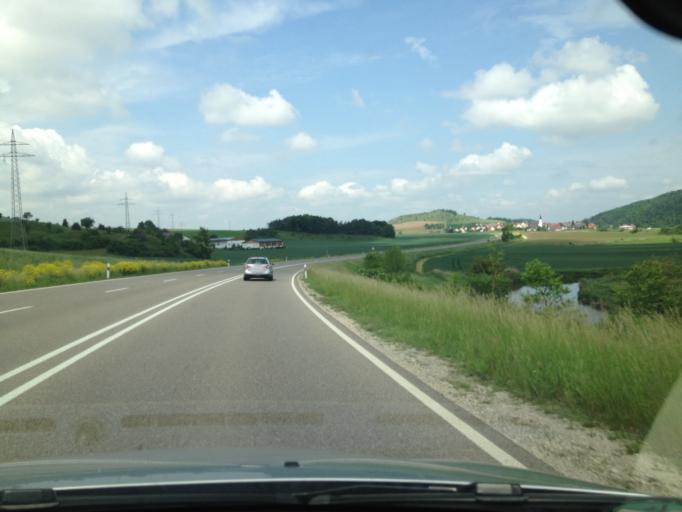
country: DE
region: Bavaria
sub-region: Swabia
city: Harburg
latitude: 48.7905
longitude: 10.6679
